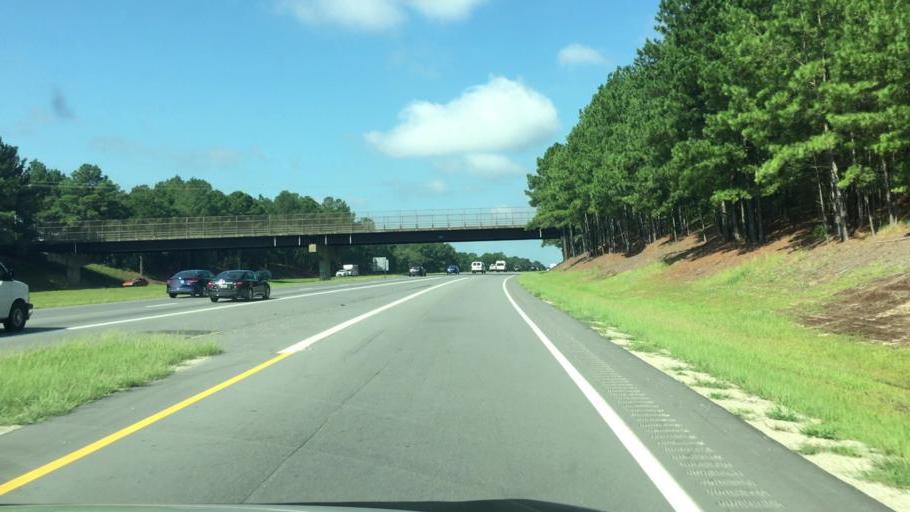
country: US
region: North Carolina
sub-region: Cumberland County
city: Fayetteville
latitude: 34.9733
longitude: -78.8639
